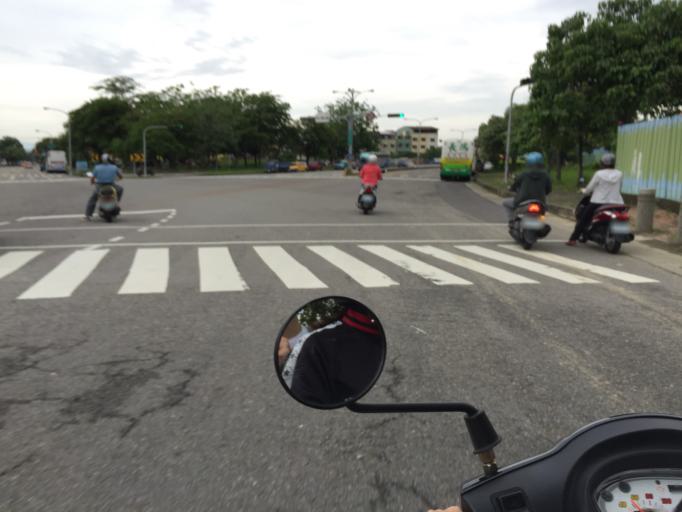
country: TW
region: Taiwan
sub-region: Taichung City
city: Taichung
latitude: 24.1424
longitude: 120.6967
